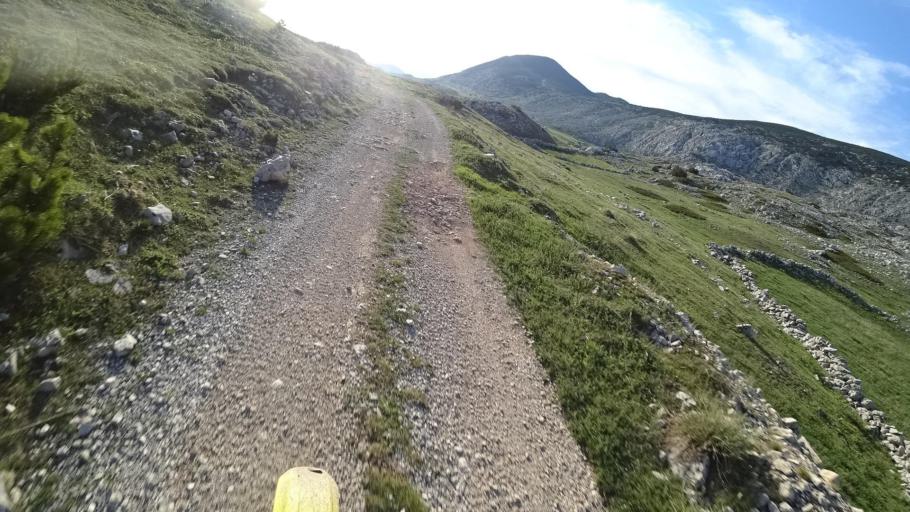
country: BA
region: Federation of Bosnia and Herzegovina
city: Kocerin
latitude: 43.5746
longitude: 17.5308
